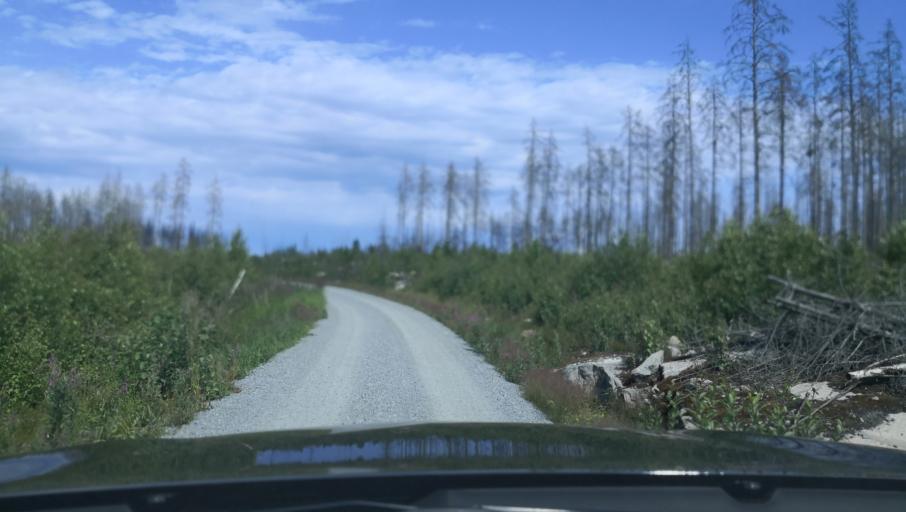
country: SE
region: Vaestmanland
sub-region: Surahammars Kommun
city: Ramnas
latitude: 59.9192
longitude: 16.1602
